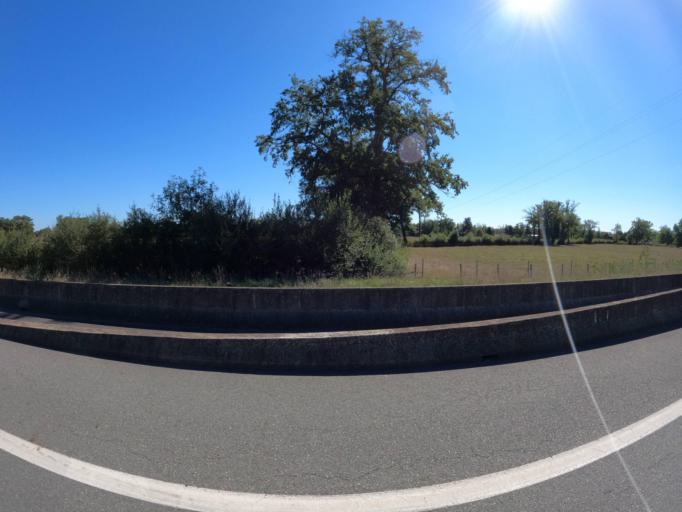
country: FR
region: Limousin
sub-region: Departement de la Creuse
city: Gouzon
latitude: 46.1965
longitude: 2.2294
